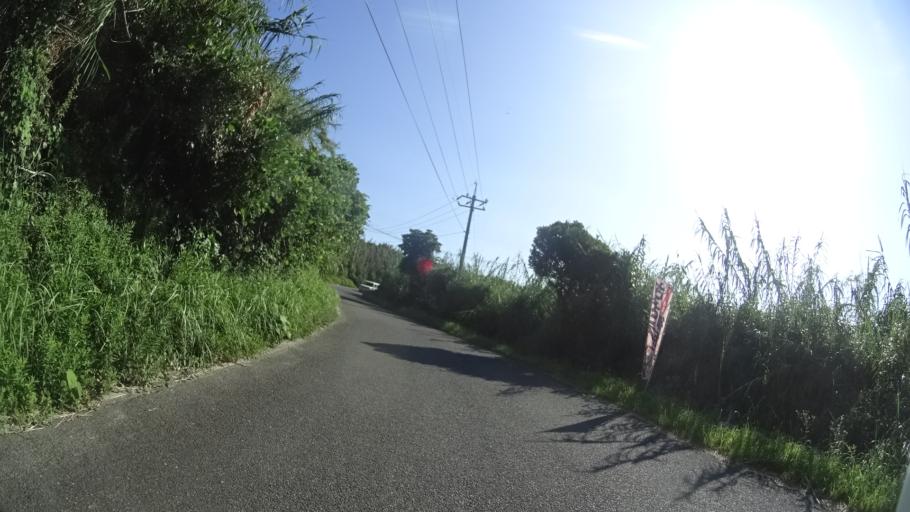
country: JP
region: Yamaguchi
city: Nagato
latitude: 34.3499
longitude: 130.8425
